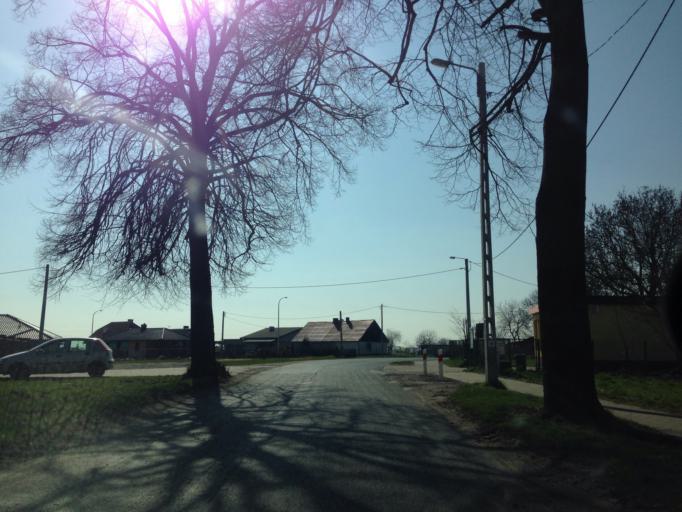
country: PL
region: Lower Silesian Voivodeship
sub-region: Powiat olesnicki
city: Bierutow
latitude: 51.1908
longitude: 17.4899
